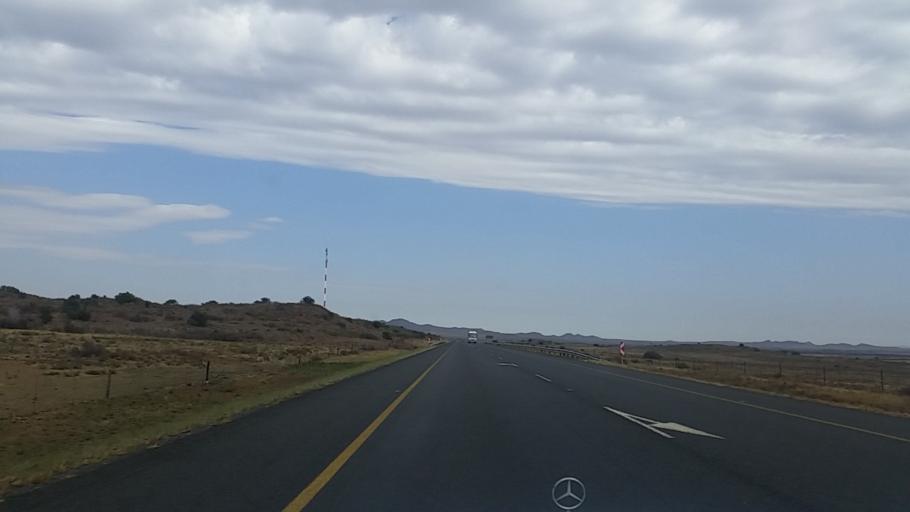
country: ZA
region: Northern Cape
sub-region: Pixley ka Seme District Municipality
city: Colesberg
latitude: -30.6177
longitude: 25.3099
